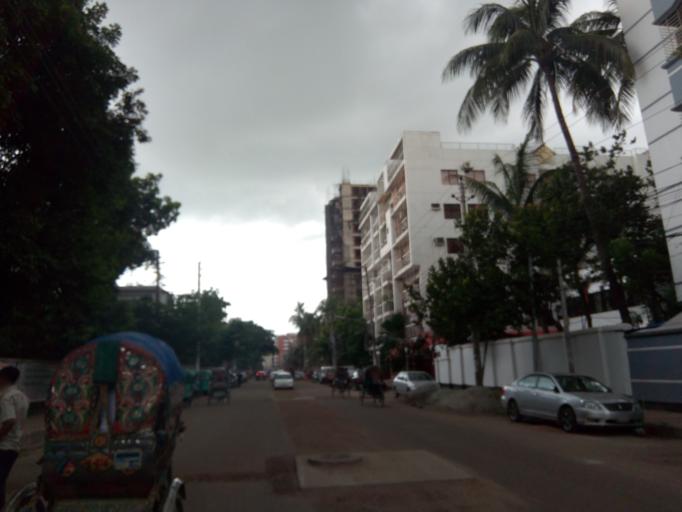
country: BD
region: Dhaka
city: Azimpur
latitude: 23.7677
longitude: 90.3683
